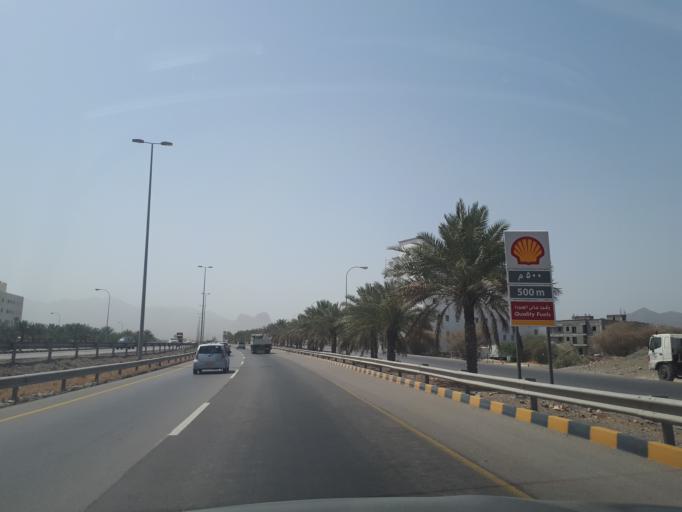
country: OM
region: Muhafazat ad Dakhiliyah
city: Bidbid
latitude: 23.5259
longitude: 58.1890
